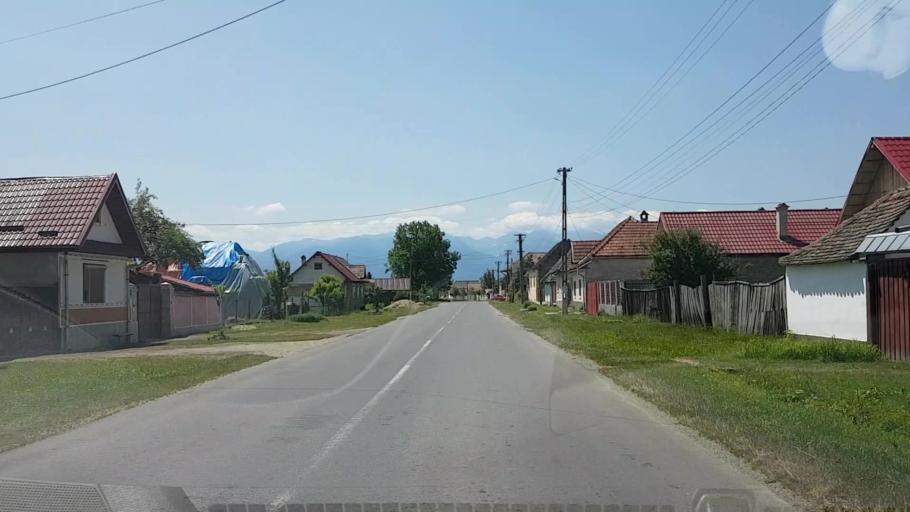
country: RO
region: Brasov
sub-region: Comuna Voila
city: Voila
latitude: 45.8443
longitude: 24.8330
